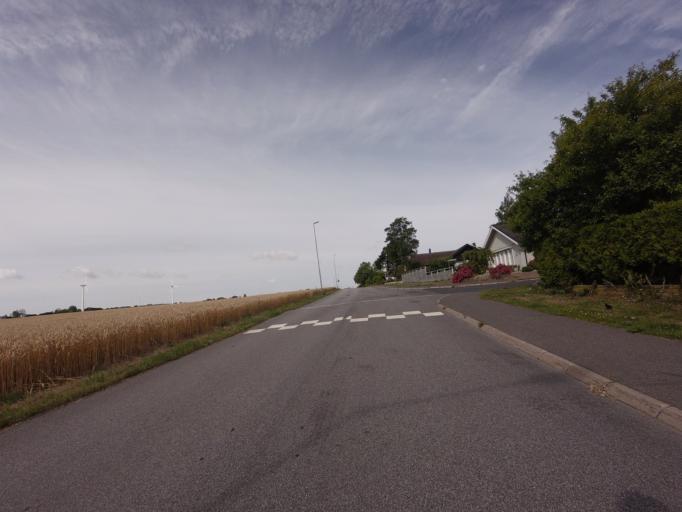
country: SE
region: Skane
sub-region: Simrishamns Kommun
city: Simrishamn
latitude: 55.5404
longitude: 14.3470
